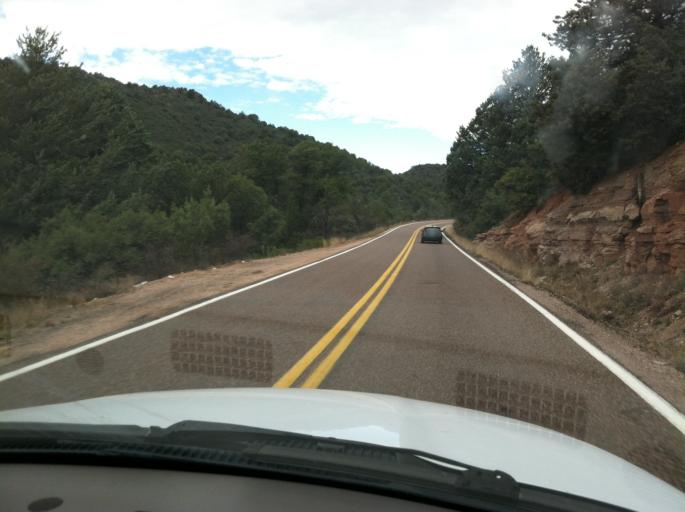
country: US
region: Arizona
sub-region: Gila County
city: Payson
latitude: 34.3143
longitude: -111.3695
